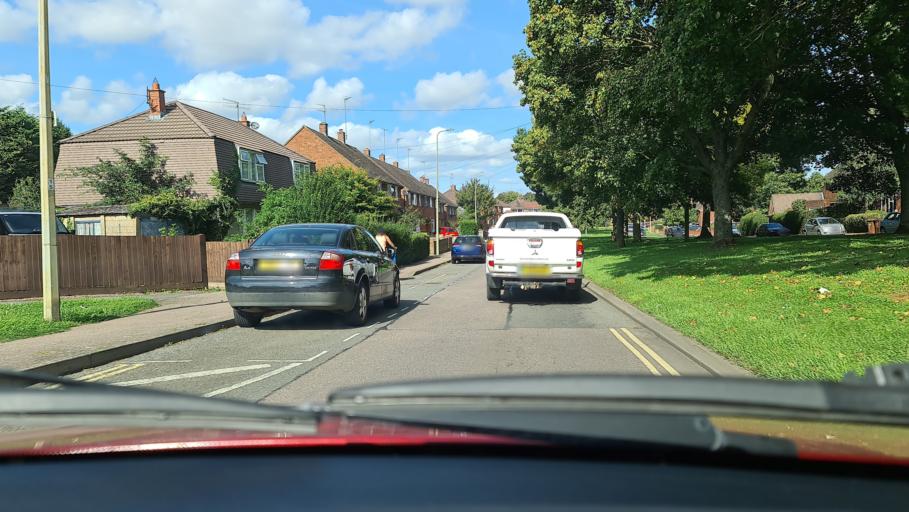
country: GB
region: England
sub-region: Oxfordshire
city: Banbury
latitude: 52.0637
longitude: -1.3519
